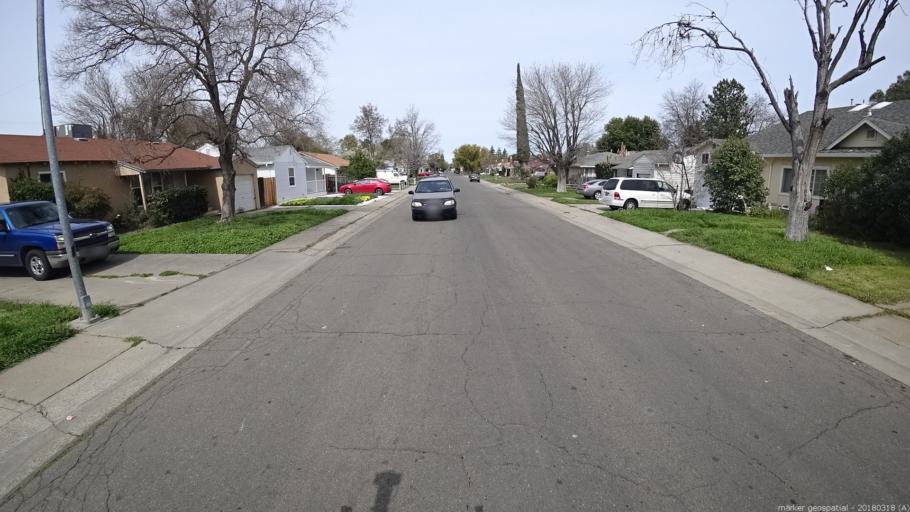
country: US
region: California
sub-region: Sacramento County
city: Parkway
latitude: 38.5178
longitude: -121.4502
